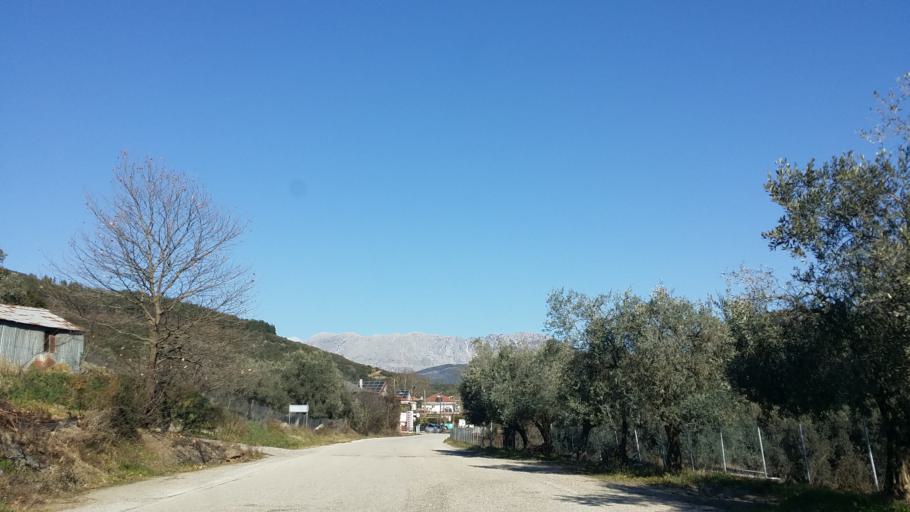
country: GR
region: West Greece
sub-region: Nomos Aitolias kai Akarnanias
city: Sardinia
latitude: 38.8866
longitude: 21.3456
